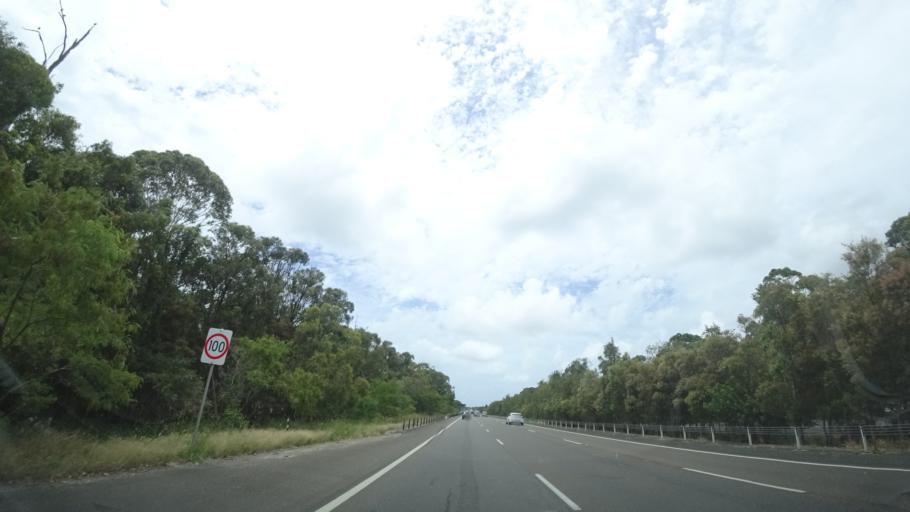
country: AU
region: Queensland
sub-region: Sunshine Coast
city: Mooloolaba
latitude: -26.6788
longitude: 153.0999
